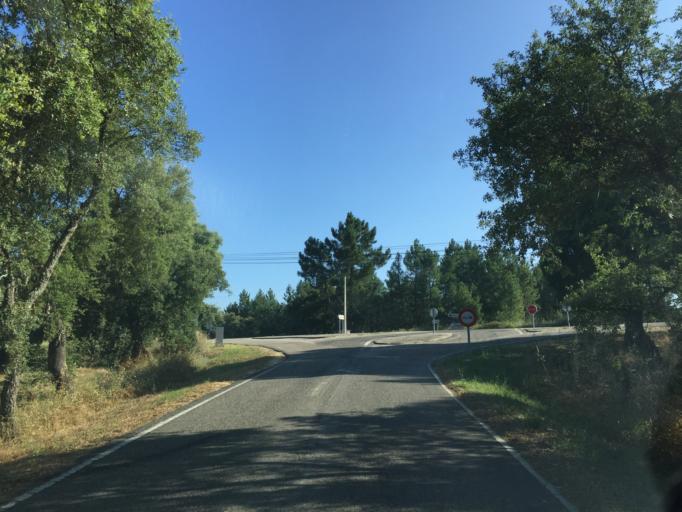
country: PT
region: Santarem
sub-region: Abrantes
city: Alferrarede
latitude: 39.5322
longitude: -8.1372
